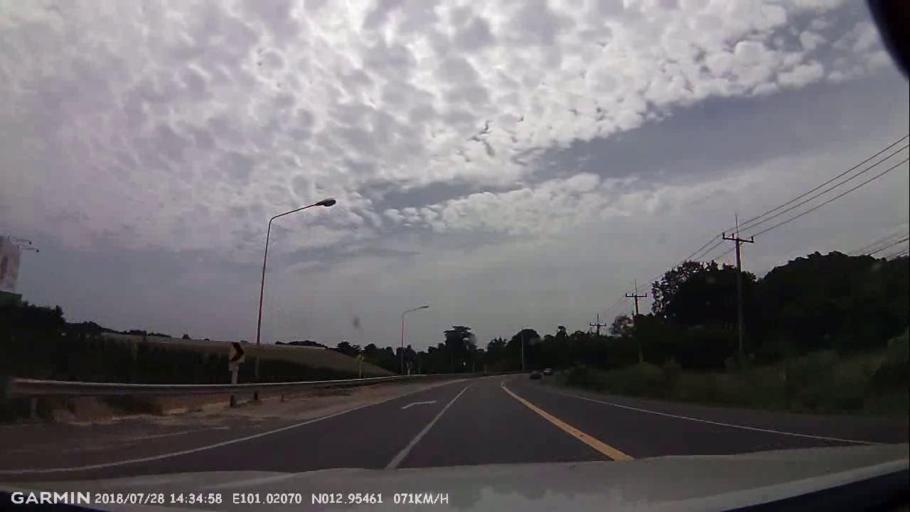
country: TH
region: Chon Buri
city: Ban Talat Bueng
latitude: 12.9544
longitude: 101.0205
